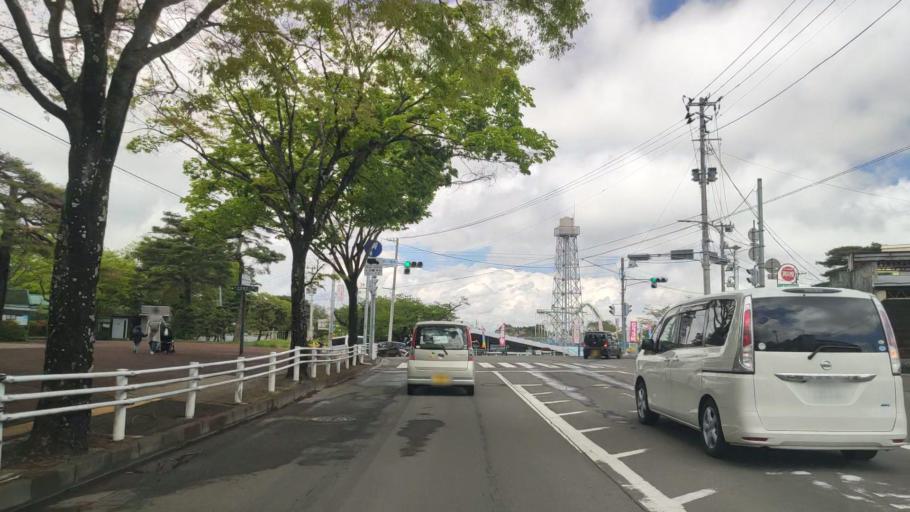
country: JP
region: Miyagi
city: Sendai
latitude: 38.2449
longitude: 140.8469
